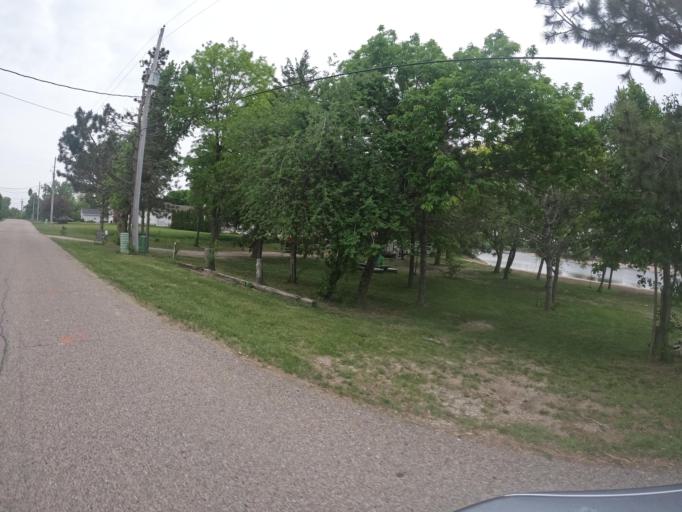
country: US
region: Nebraska
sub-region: Sarpy County
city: Offutt Air Force Base
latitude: 41.0542
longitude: -95.9520
